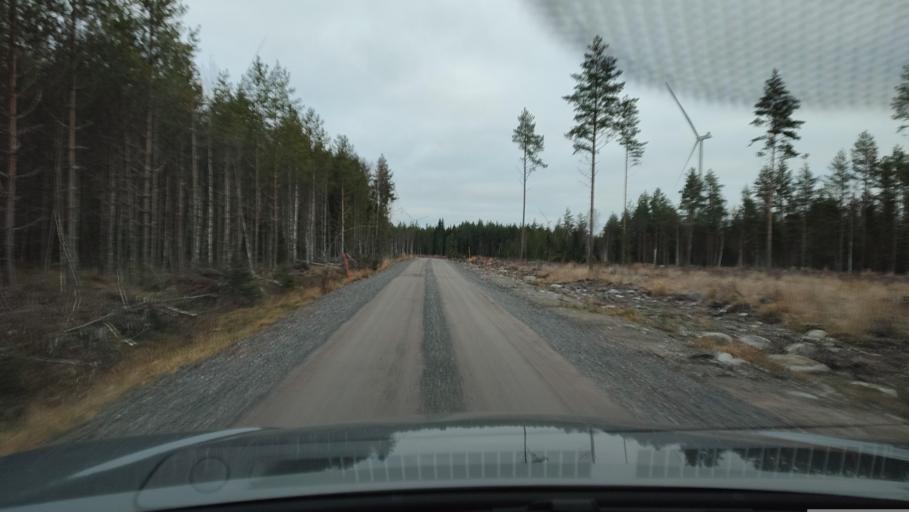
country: FI
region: Southern Ostrobothnia
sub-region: Suupohja
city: Karijoki
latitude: 62.1823
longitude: 21.5603
